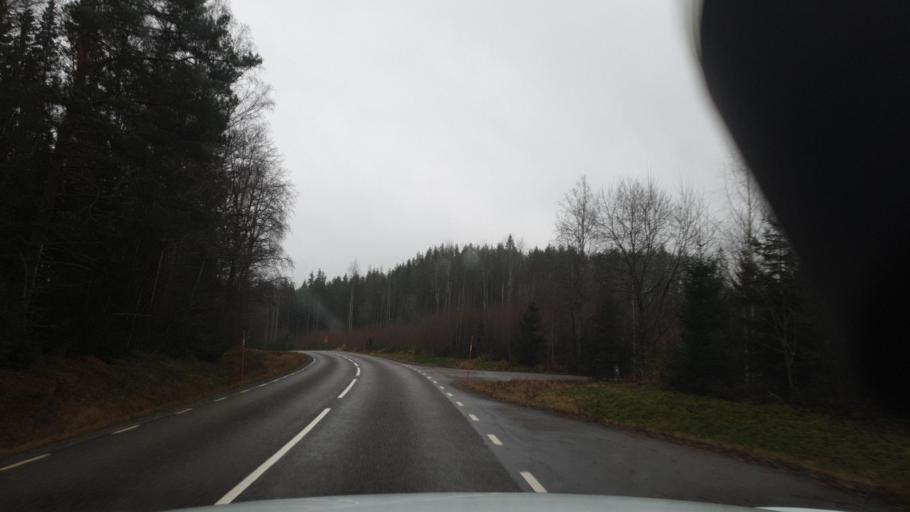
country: SE
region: Vaermland
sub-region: Eda Kommun
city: Amotfors
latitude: 59.7372
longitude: 12.3852
